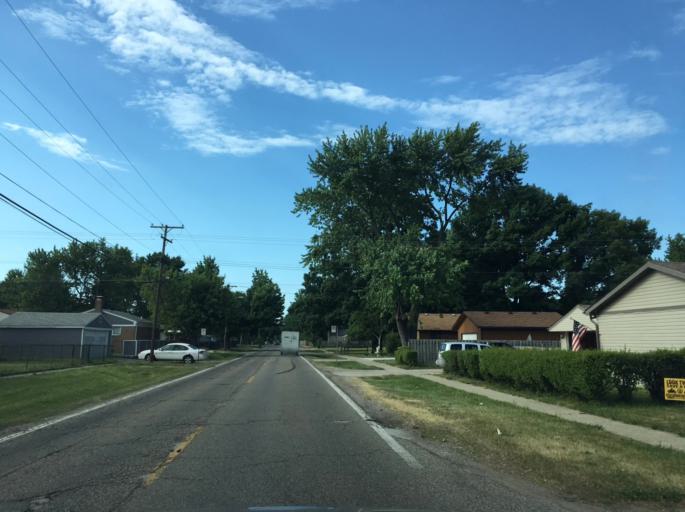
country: US
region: Michigan
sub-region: Macomb County
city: Fraser
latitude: 42.5410
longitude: -82.9196
